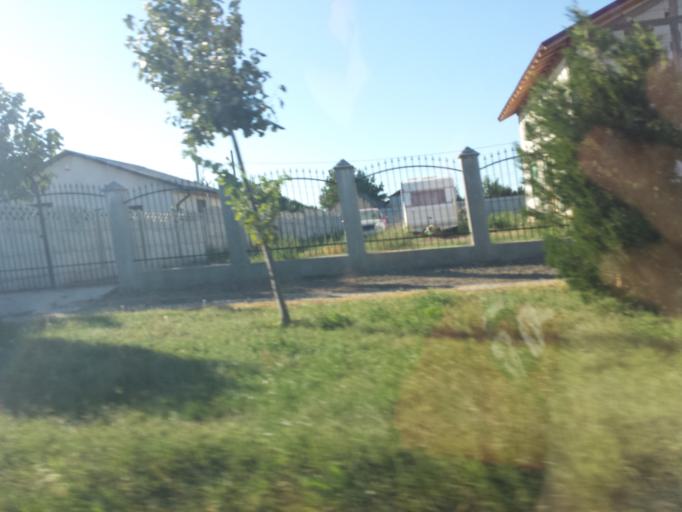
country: RO
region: Ialomita
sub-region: Comuna Ograda
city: Ograda
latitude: 44.6245
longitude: 27.5896
